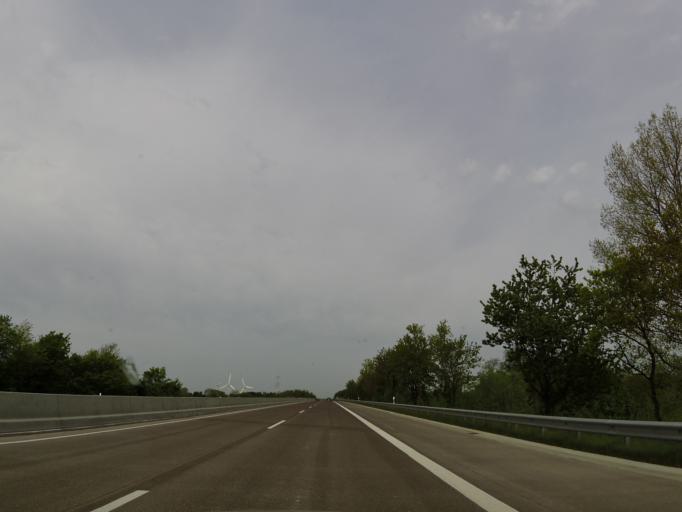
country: DE
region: Schleswig-Holstein
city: Horst
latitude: 53.8204
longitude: 9.6497
